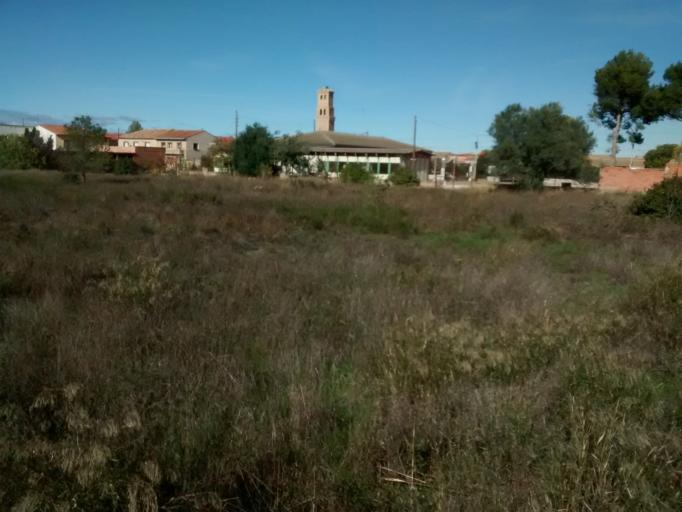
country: ES
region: Aragon
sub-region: Provincia de Zaragoza
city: Villanueva de Gallego
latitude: 41.7585
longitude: -0.7977
